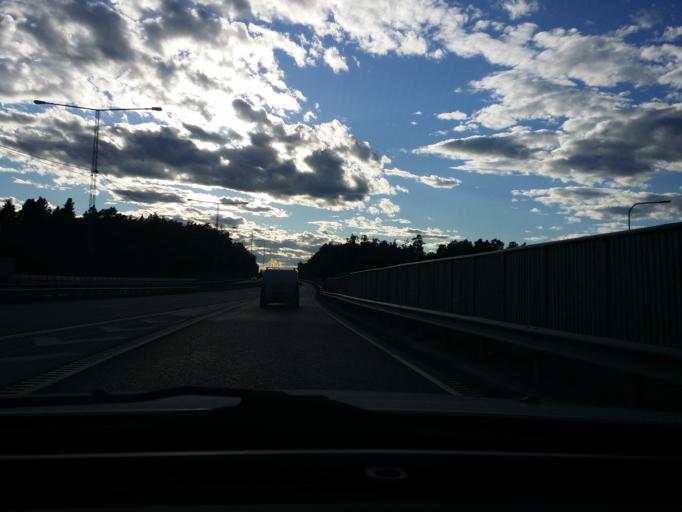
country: SE
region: Stockholm
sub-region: Upplands-Bro Kommun
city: Kungsaengen
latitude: 59.4738
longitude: 17.8066
